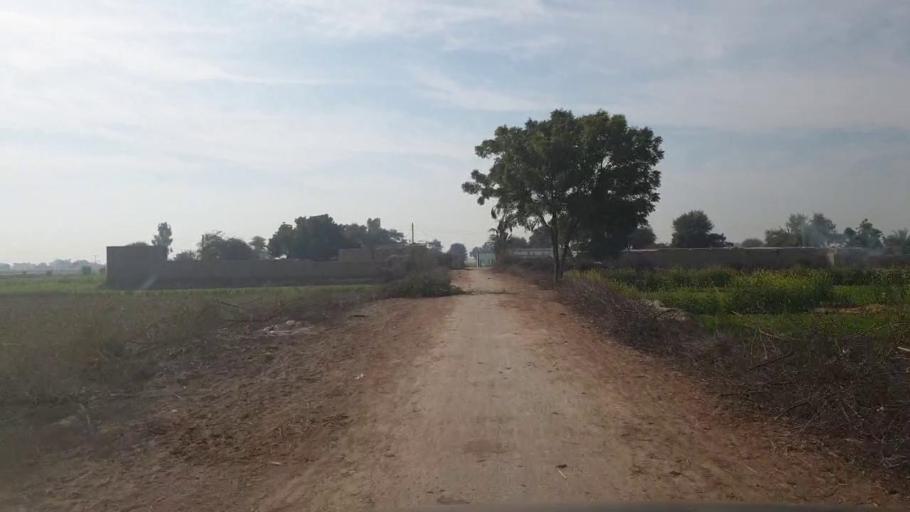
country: PK
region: Sindh
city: Shahpur Chakar
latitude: 26.1828
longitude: 68.5929
